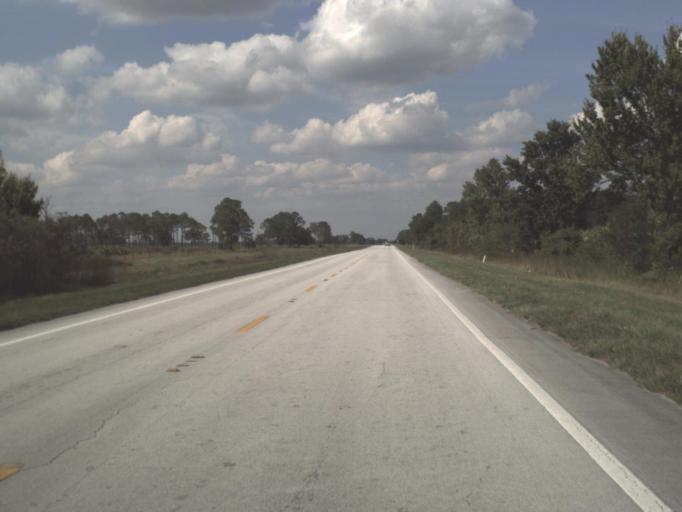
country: US
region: Florida
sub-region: Indian River County
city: Fellsmere
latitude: 27.6097
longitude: -80.8540
